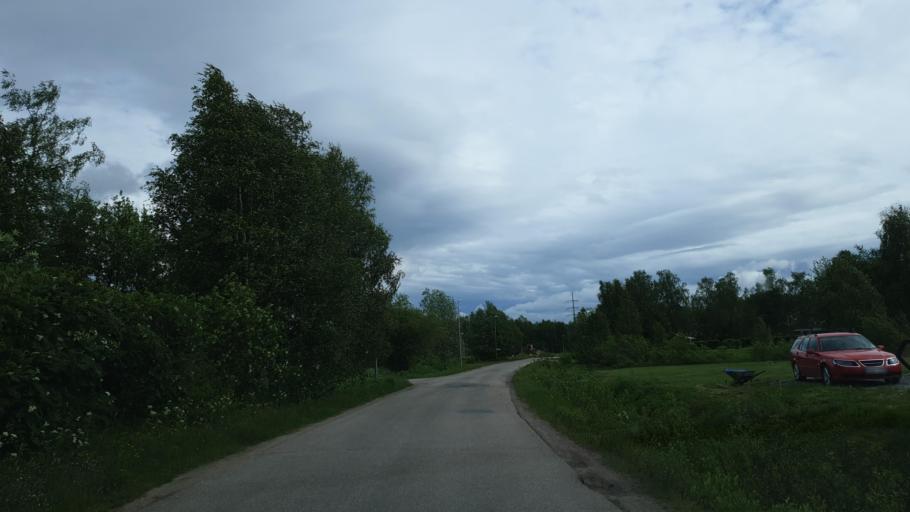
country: SE
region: Norrbotten
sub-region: Gallivare Kommun
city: Gaellivare
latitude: 67.1315
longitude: 20.6421
